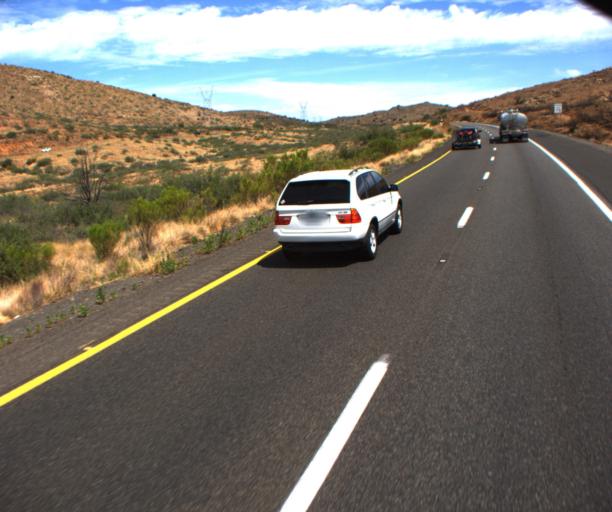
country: US
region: Arizona
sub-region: Yavapai County
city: Cordes Lakes
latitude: 34.2932
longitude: -112.1240
